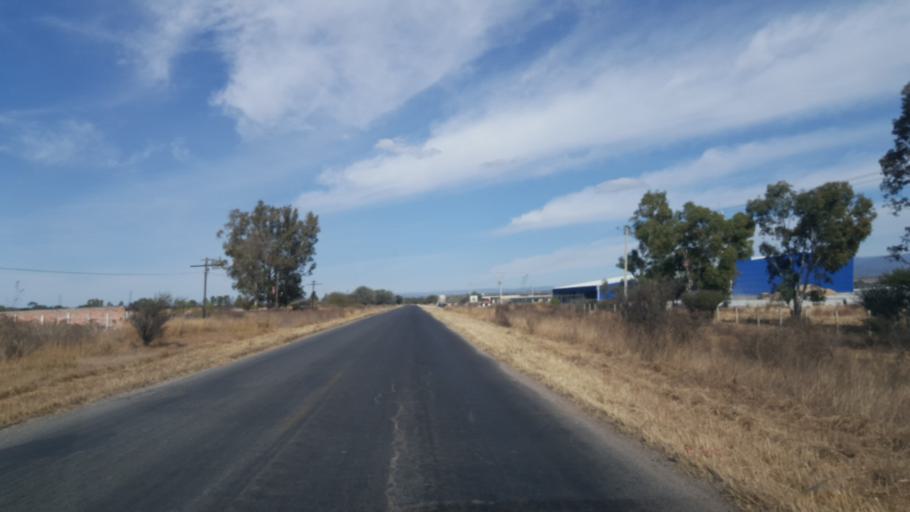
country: MX
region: Jalisco
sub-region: Lagos de Moreno
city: Geovillas Laureles del Campanario
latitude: 21.2914
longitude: -101.9311
